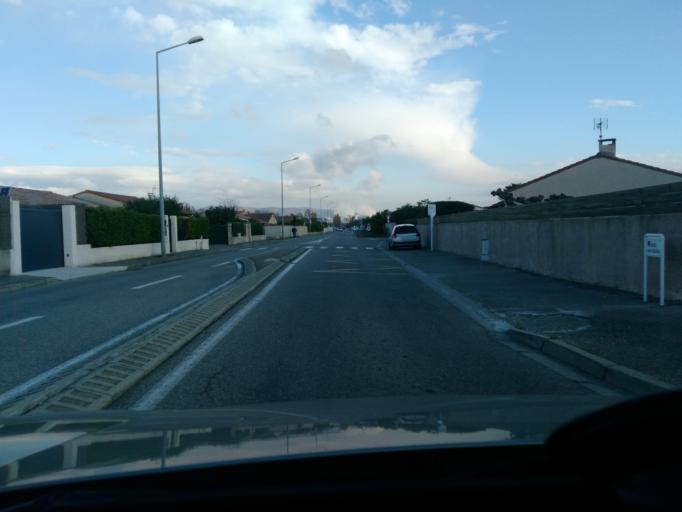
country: FR
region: Rhone-Alpes
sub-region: Departement de la Drome
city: Montelimar
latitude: 44.5671
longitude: 4.7409
